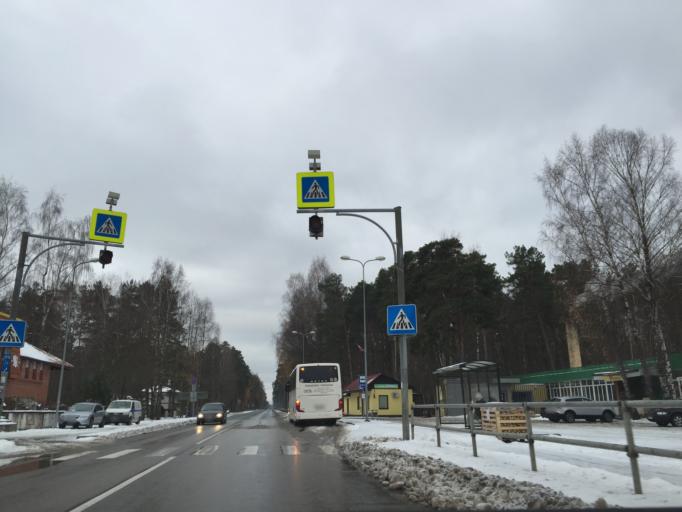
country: LV
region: Saulkrastu
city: Saulkrasti
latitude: 57.2560
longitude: 24.4146
